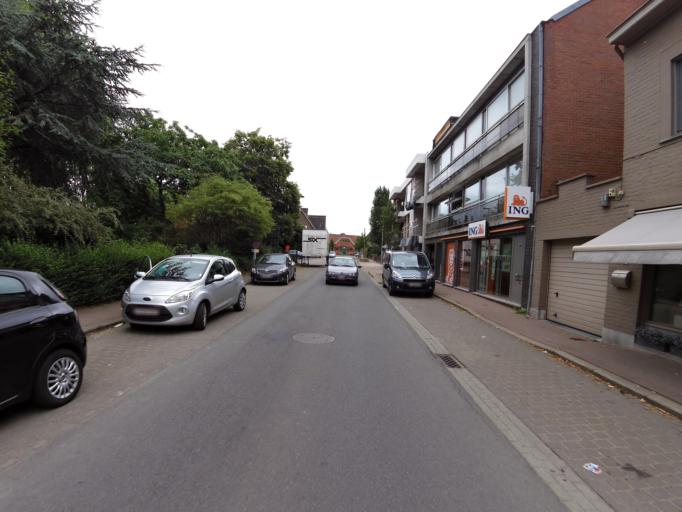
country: BE
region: Flanders
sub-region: Provincie West-Vlaanderen
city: Kortemark
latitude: 51.0265
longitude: 3.0438
